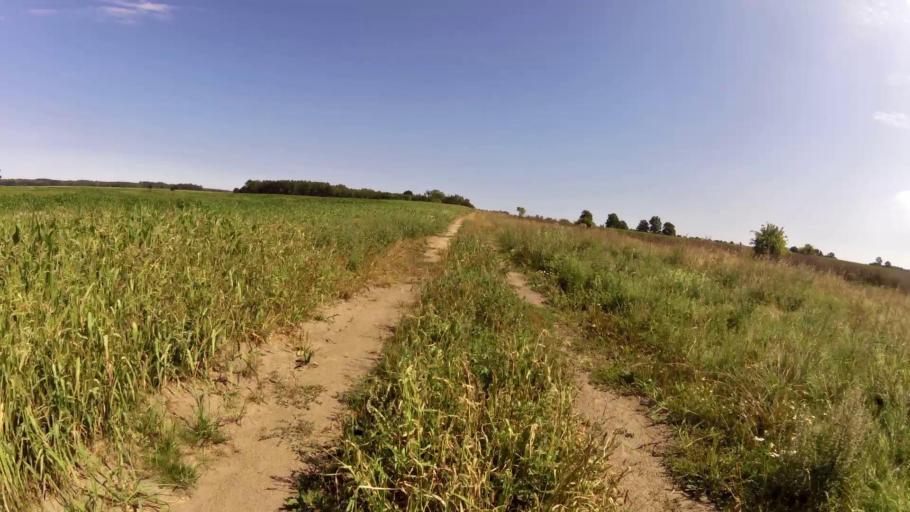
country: PL
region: West Pomeranian Voivodeship
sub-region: Powiat stargardzki
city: Dobrzany
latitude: 53.2832
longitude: 15.4447
